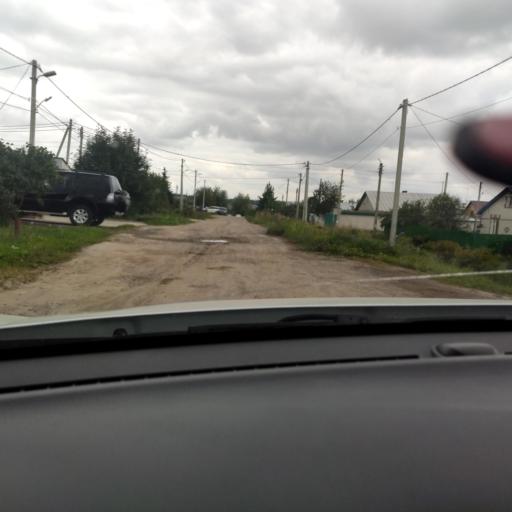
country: RU
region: Tatarstan
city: Vysokaya Gora
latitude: 55.8162
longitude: 49.2574
